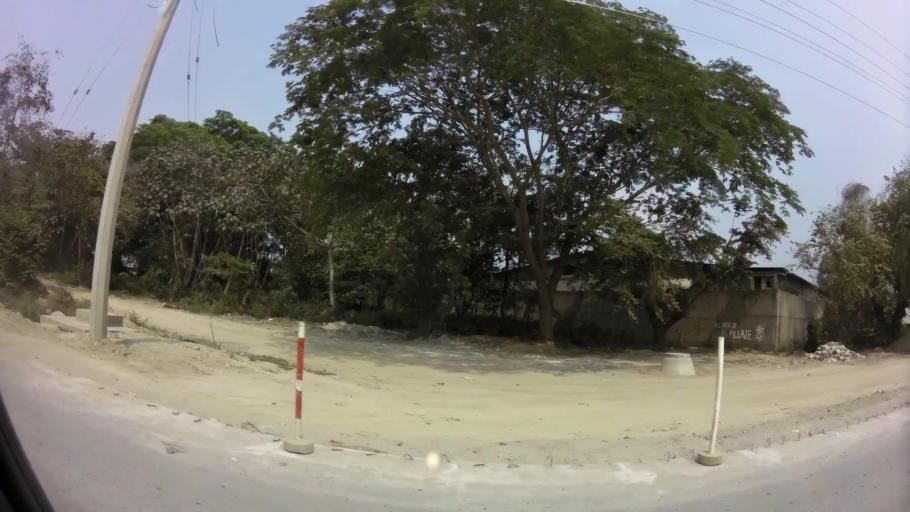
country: HN
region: Cortes
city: San Pedro Sula
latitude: 15.5514
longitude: -87.9974
